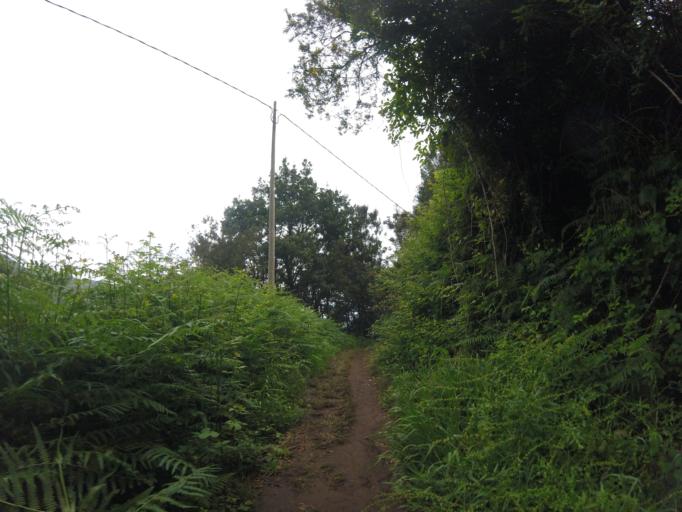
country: ES
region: Canary Islands
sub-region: Provincia de Santa Cruz de Tenerife
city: Tegueste
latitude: 28.5419
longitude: -16.2789
